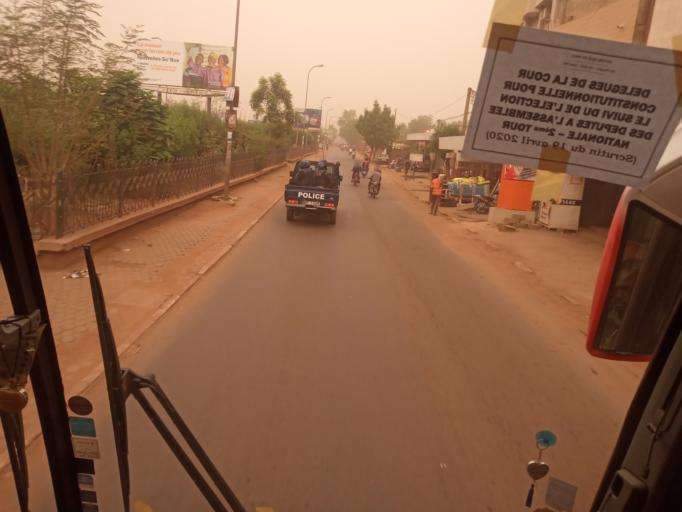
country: ML
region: Bamako
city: Bamako
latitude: 12.6525
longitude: -7.9854
